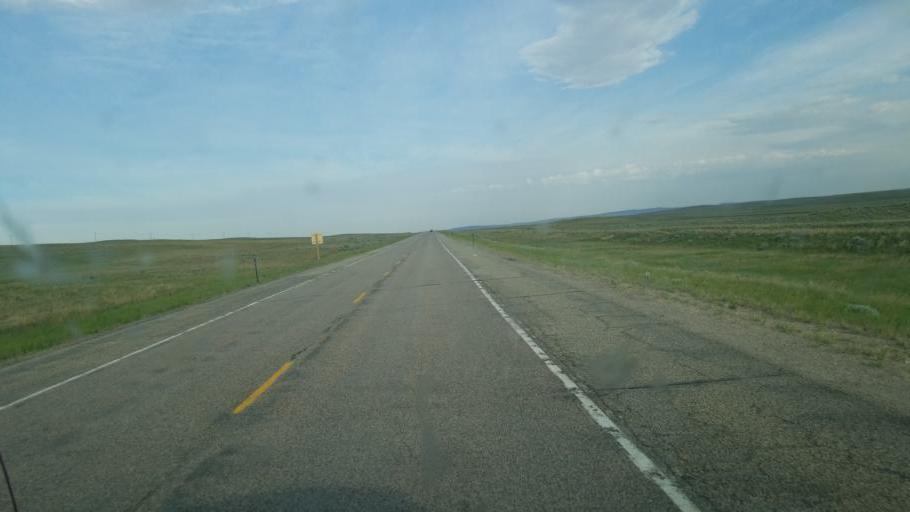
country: US
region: Wyoming
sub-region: Natrona County
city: Mills
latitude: 43.0344
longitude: -106.8700
